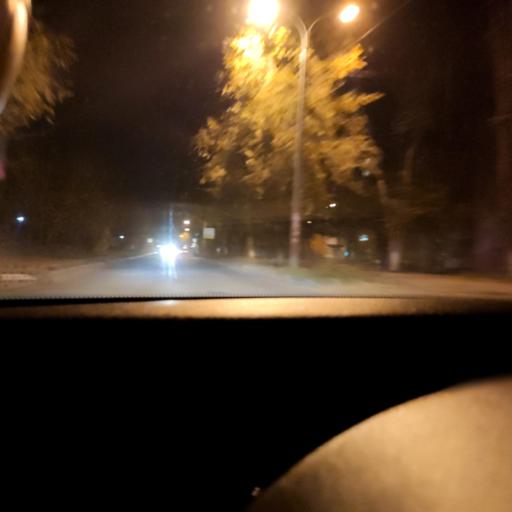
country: RU
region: Samara
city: Samara
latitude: 53.2426
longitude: 50.2556
